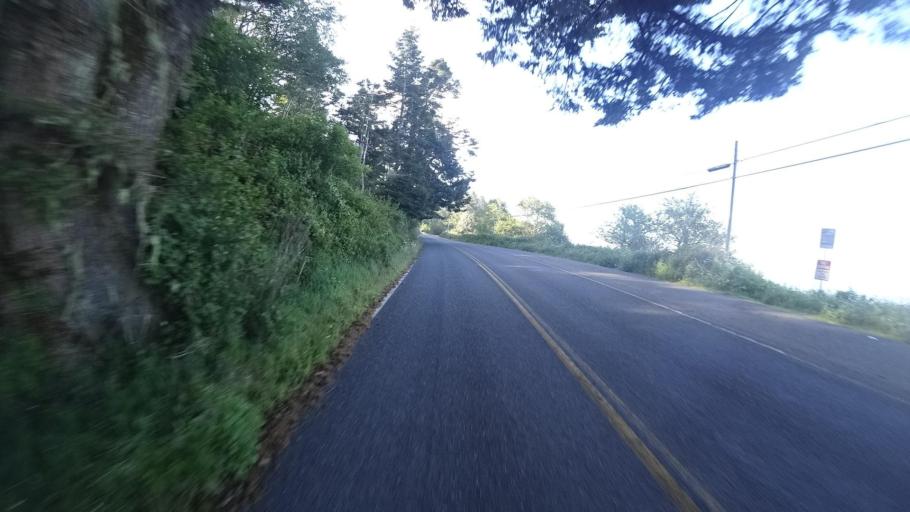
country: US
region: California
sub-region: Humboldt County
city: Westhaven-Moonstone
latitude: 41.1006
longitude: -124.1591
